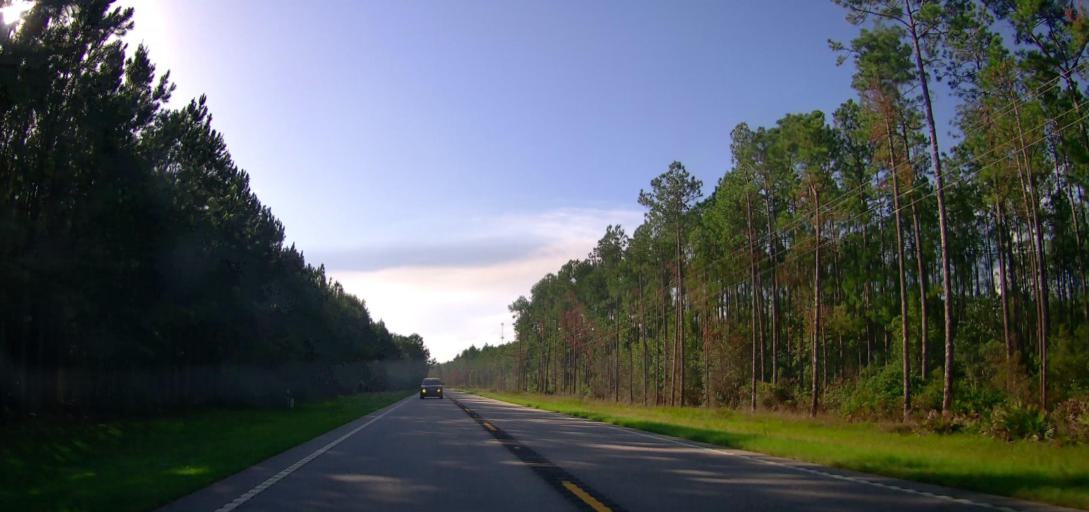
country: US
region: Georgia
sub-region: Coffee County
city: Nicholls
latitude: 31.4474
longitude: -82.7238
